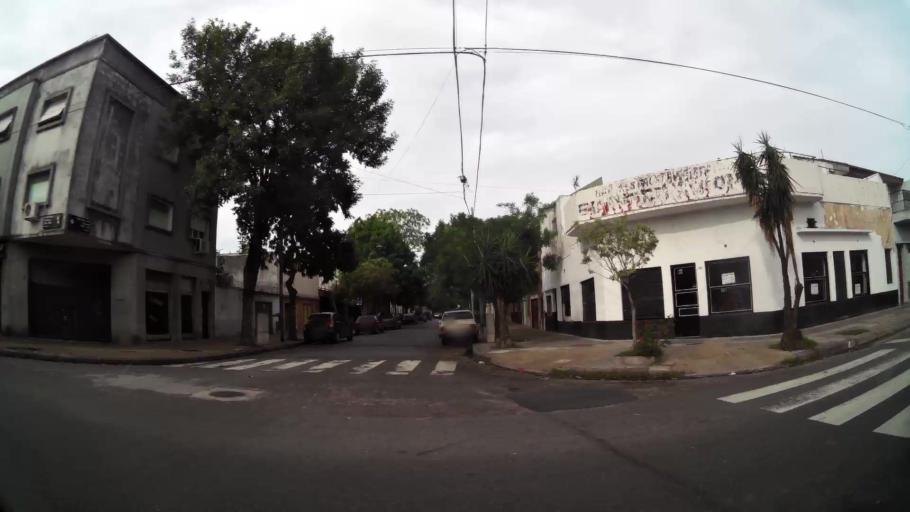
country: AR
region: Buenos Aires F.D.
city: Villa Lugano
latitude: -34.6467
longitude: -58.4297
